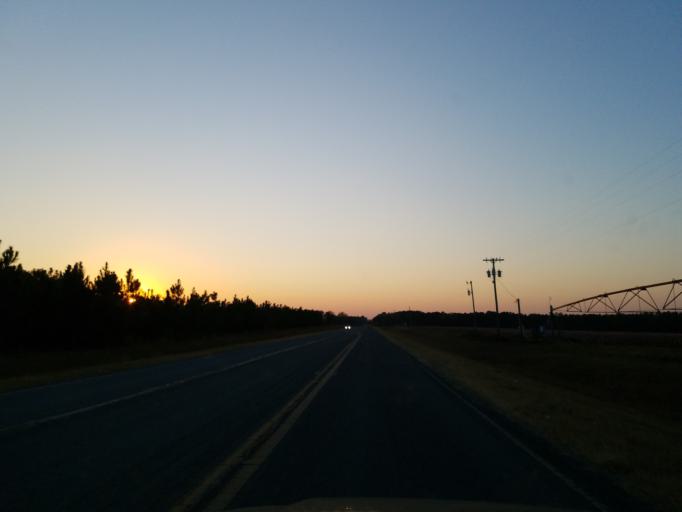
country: US
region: Georgia
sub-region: Ben Hill County
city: Fitzgerald
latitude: 31.7203
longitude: -83.4114
